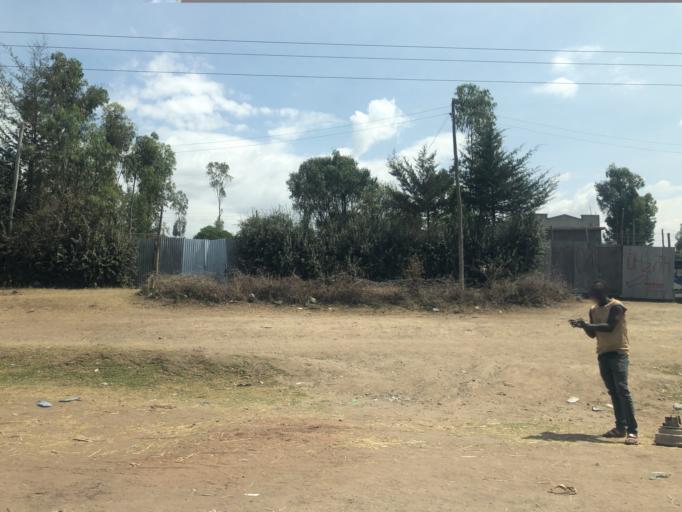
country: ET
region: Oromiya
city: Shashemene
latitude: 7.3406
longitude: 38.6694
